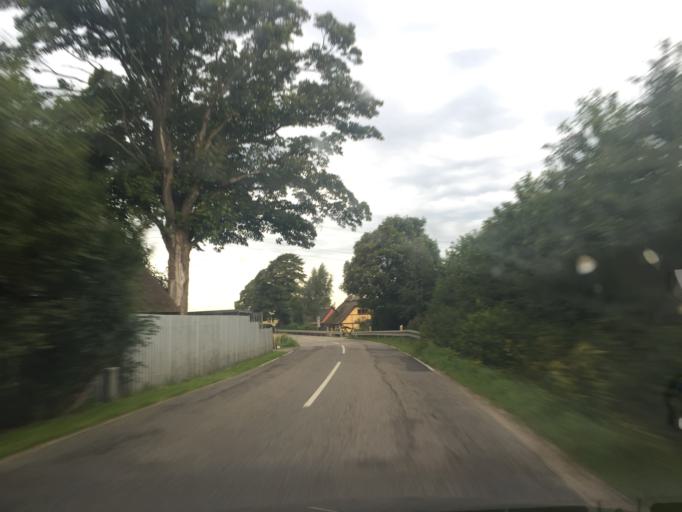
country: DK
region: Capital Region
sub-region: Egedal Kommune
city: Vekso
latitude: 55.7062
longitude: 12.2249
